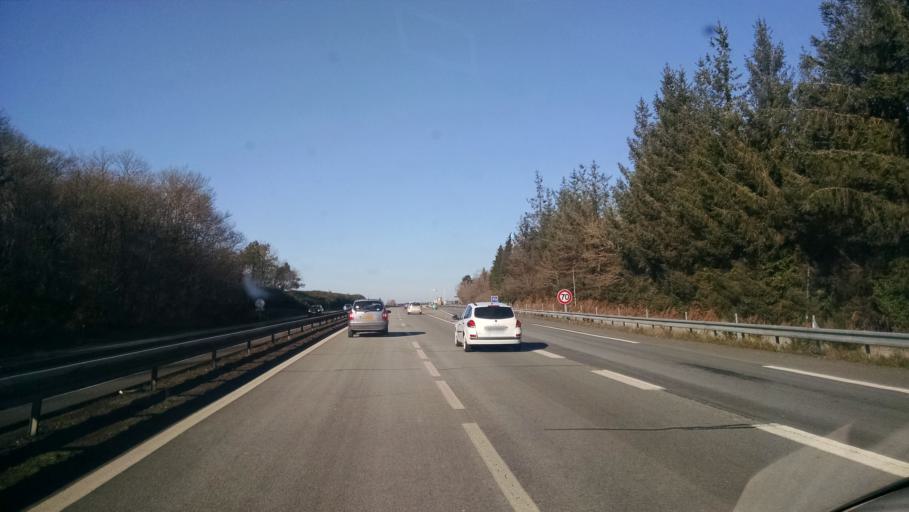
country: FR
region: Brittany
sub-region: Departement du Morbihan
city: Branderion
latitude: 47.7762
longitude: -3.1906
